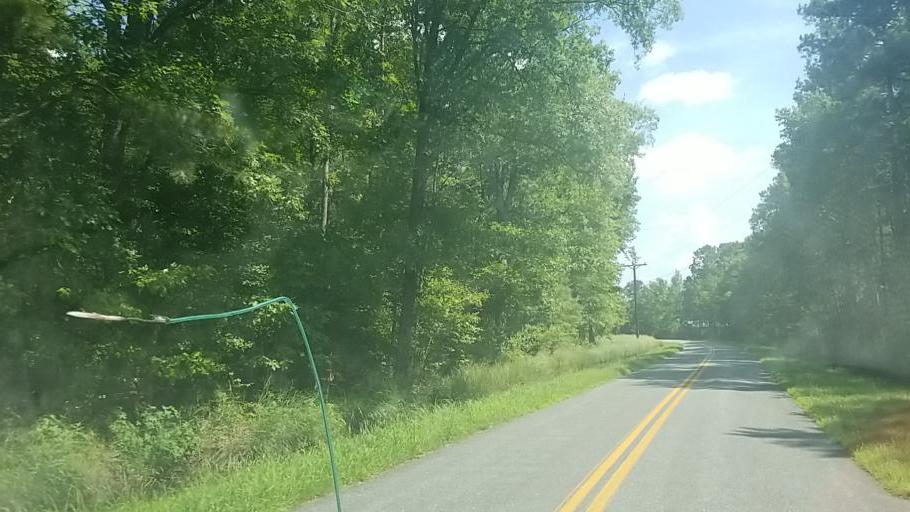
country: US
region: Maryland
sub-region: Dorchester County
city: Hurlock
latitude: 38.4315
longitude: -75.8865
